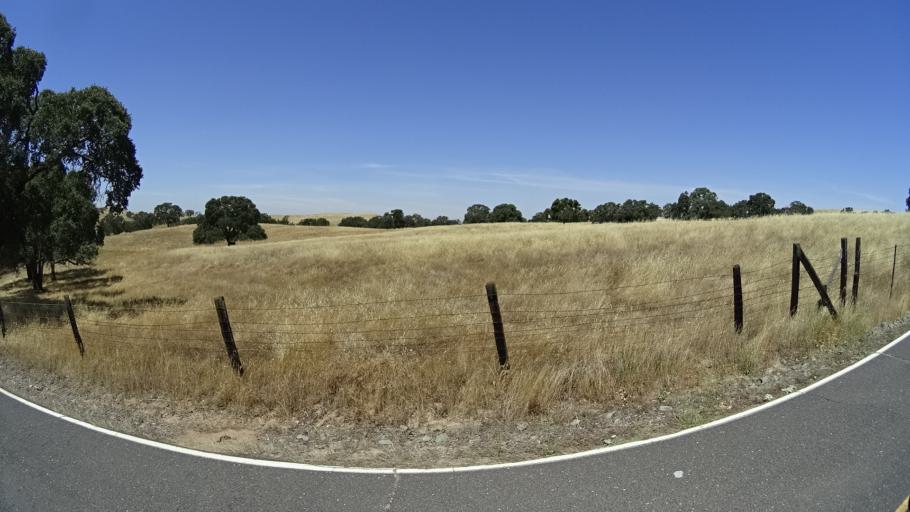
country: US
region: California
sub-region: Calaveras County
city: Rancho Calaveras
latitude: 38.1302
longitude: -120.9449
